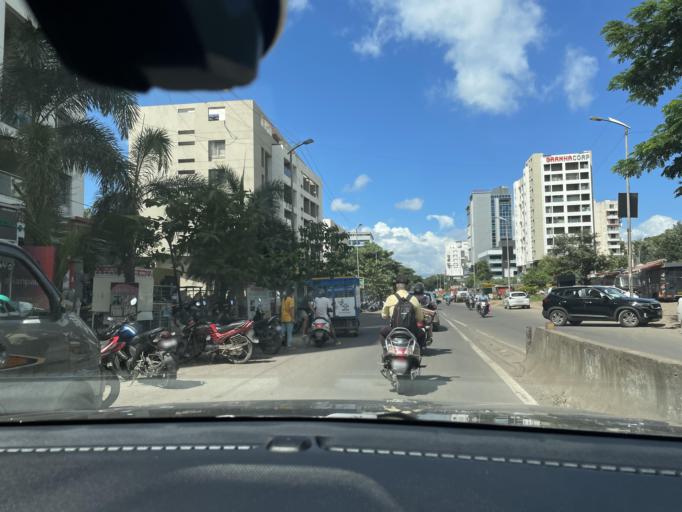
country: IN
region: Maharashtra
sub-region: Pune Division
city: Shivaji Nagar
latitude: 18.5203
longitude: 73.7789
